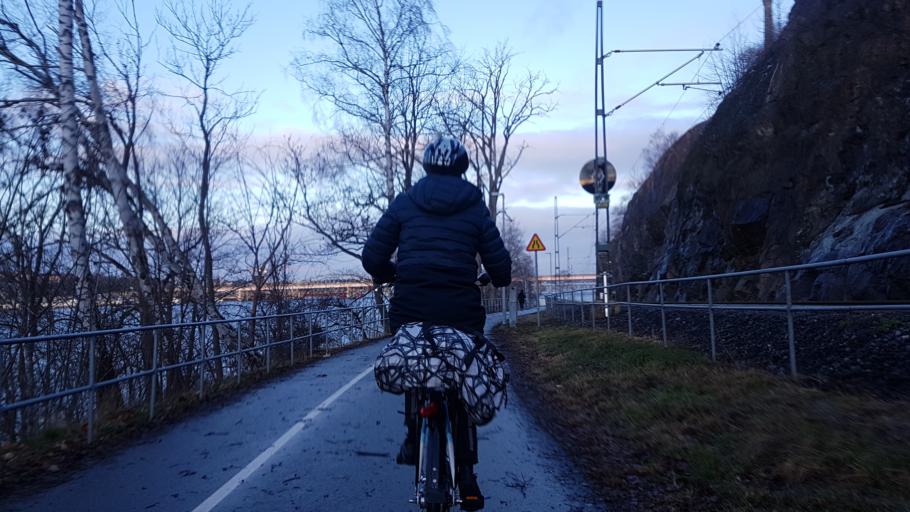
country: SE
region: Stockholm
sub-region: Lidingo
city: Lidingoe
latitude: 59.3578
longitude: 18.1226
